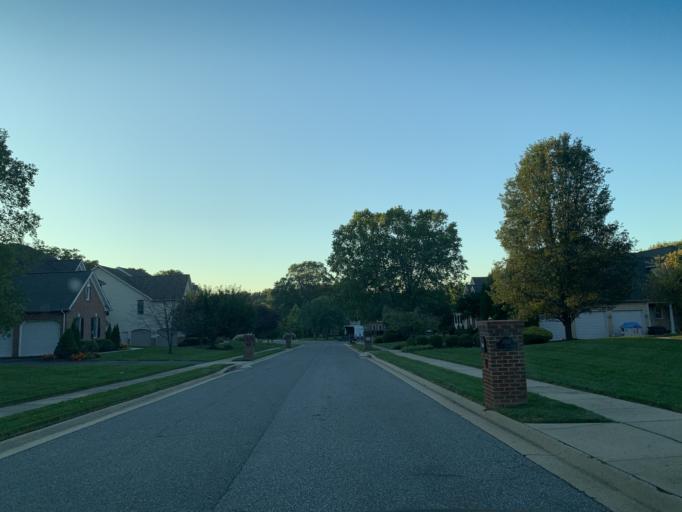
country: US
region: Maryland
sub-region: Harford County
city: Bel Air South
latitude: 39.5234
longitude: -76.3006
